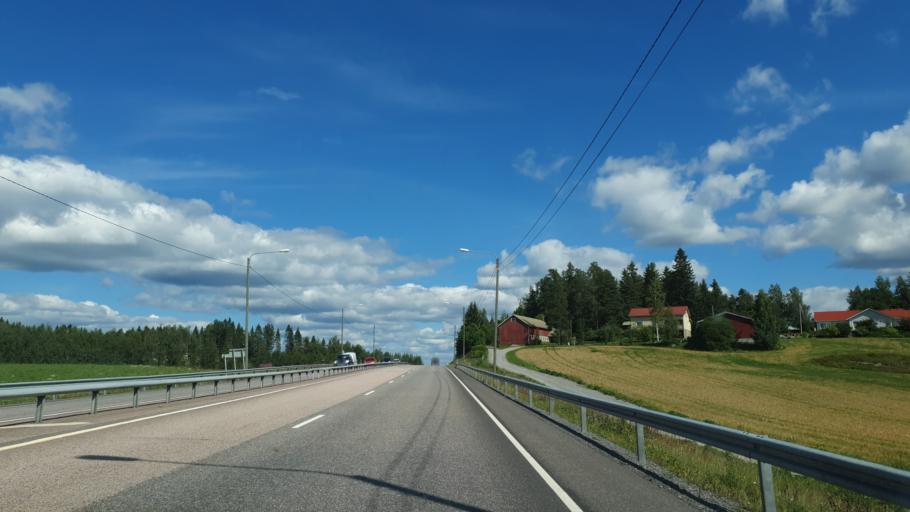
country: FI
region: Pirkanmaa
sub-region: Tampere
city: Orivesi
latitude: 61.6926
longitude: 24.4134
